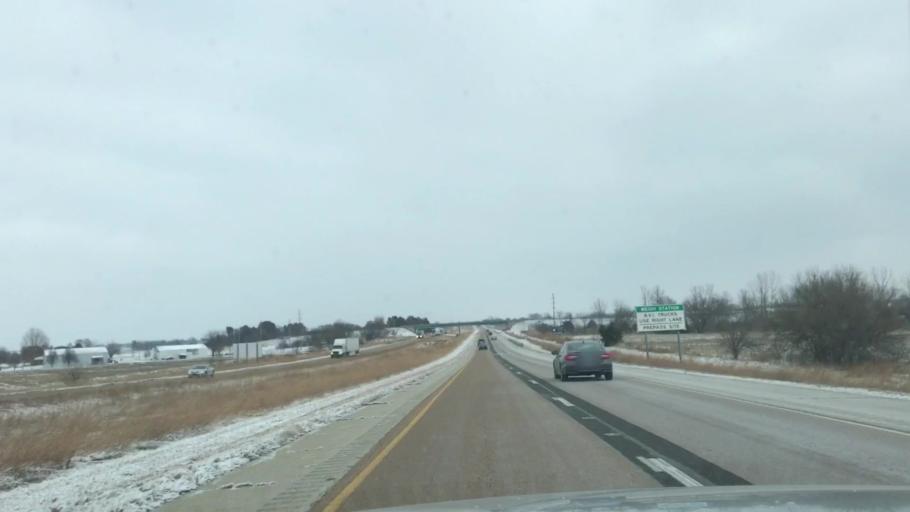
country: US
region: Illinois
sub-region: Montgomery County
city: Litchfield
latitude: 39.2008
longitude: -89.6625
